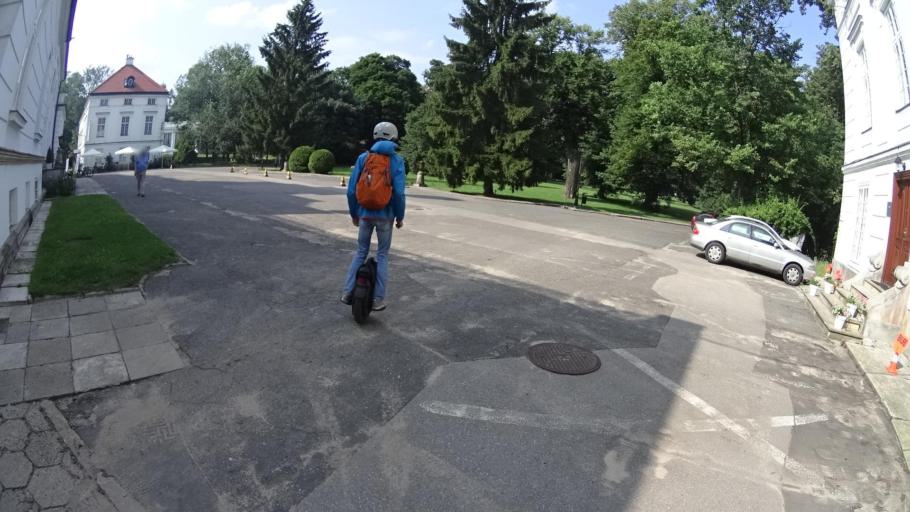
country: PL
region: Masovian Voivodeship
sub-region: Powiat legionowski
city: Jablonna
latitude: 52.3747
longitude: 20.9144
